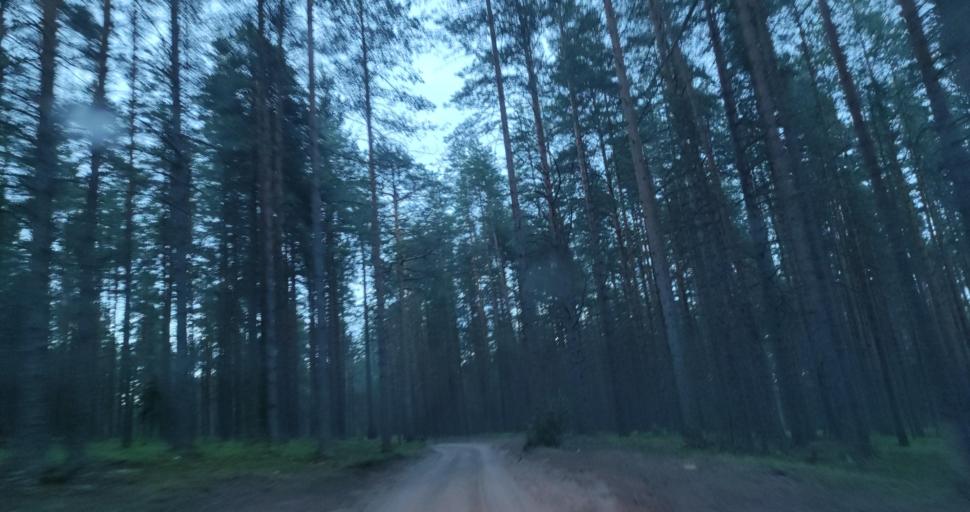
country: RU
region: Leningrad
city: Sapernoye
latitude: 60.6752
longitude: 29.9449
